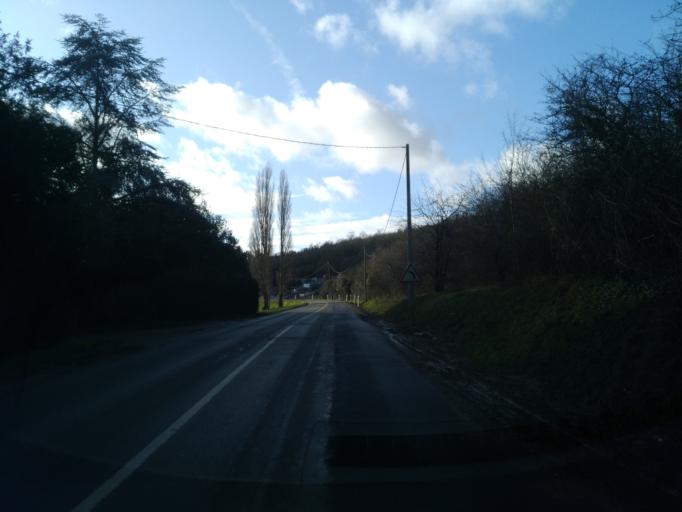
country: FR
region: Ile-de-France
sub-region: Departement des Yvelines
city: Beynes
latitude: 48.8721
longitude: 1.8723
